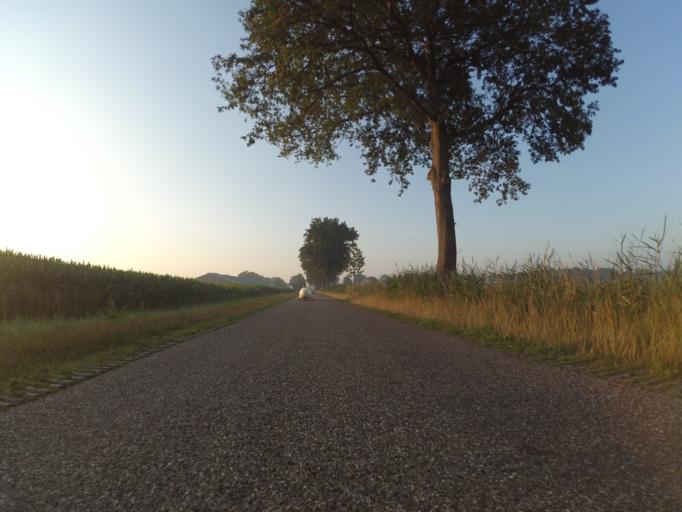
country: NL
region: Overijssel
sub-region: Gemeente Twenterand
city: Vriezenveen
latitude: 52.4051
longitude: 6.6632
